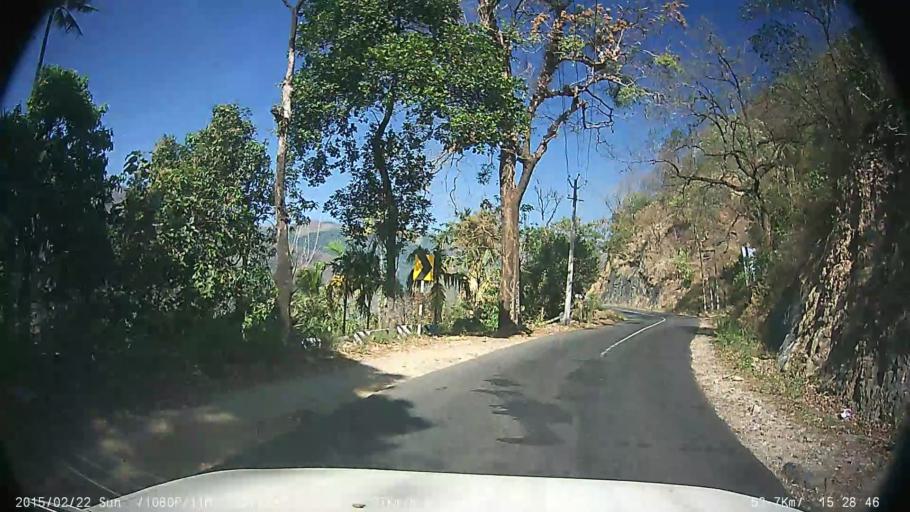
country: IN
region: Kerala
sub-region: Kottayam
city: Erattupetta
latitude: 9.5573
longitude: 76.9432
